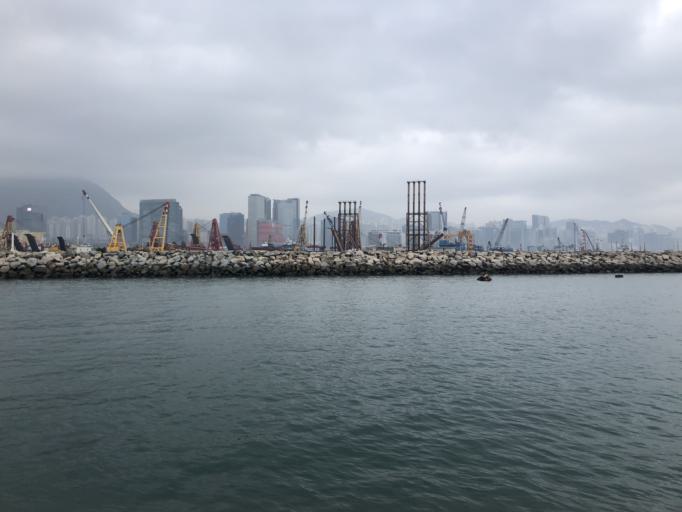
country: HK
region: Kowloon City
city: Kowloon
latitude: 22.3133
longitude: 114.1938
